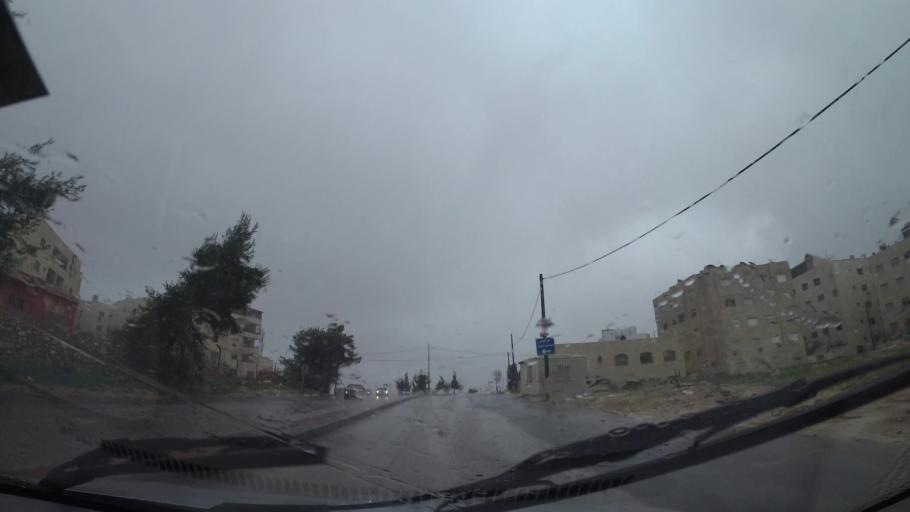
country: JO
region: Amman
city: Al Jubayhah
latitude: 32.0209
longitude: 35.8853
